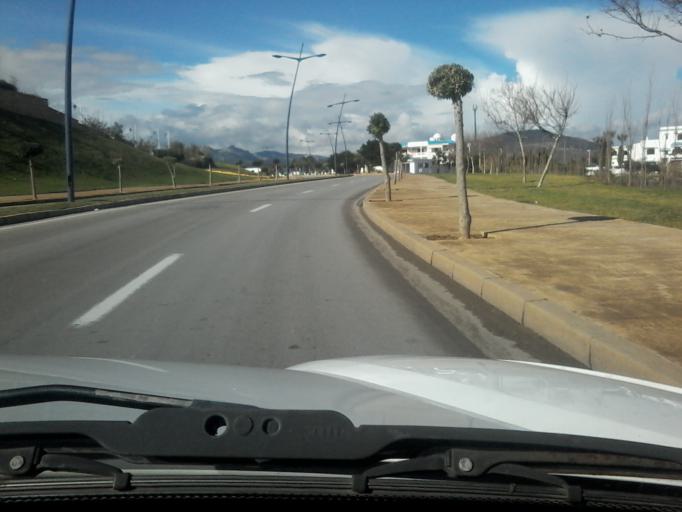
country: MA
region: Tanger-Tetouan
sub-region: Tetouan
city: Martil
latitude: 35.6941
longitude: -5.3331
